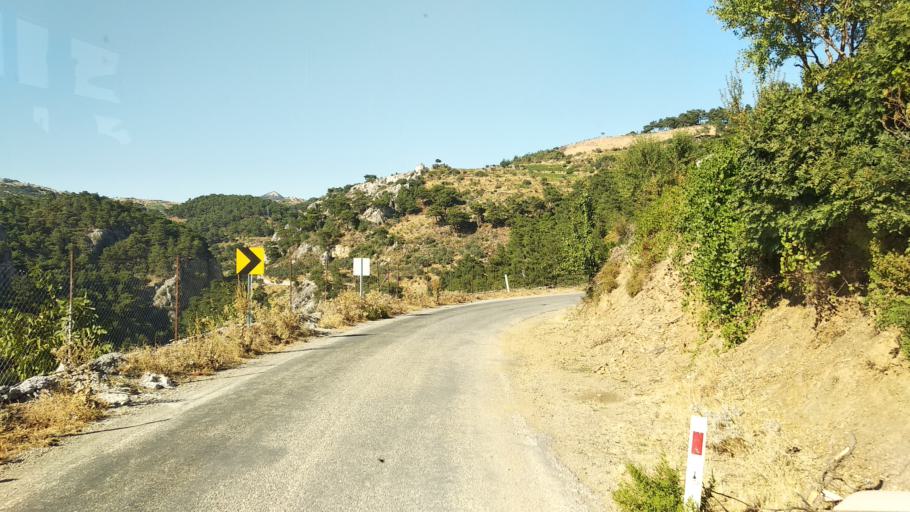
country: TR
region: Izmir
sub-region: Seferihisar
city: Seferhisar
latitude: 38.3153
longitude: 26.9555
